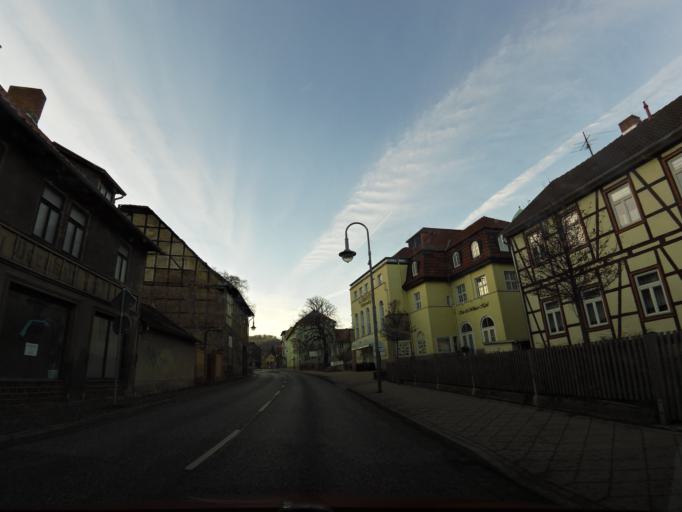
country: DE
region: Saxony-Anhalt
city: Blankenburg
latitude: 51.7905
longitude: 10.9566
